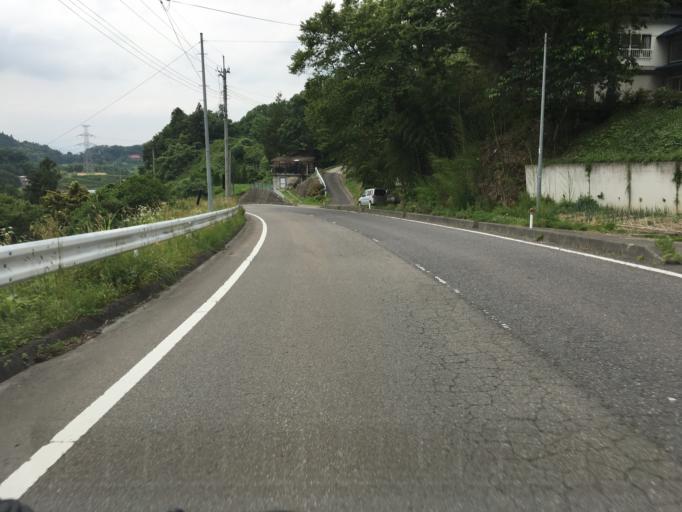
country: JP
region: Fukushima
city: Nihommatsu
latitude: 37.6073
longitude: 140.5624
